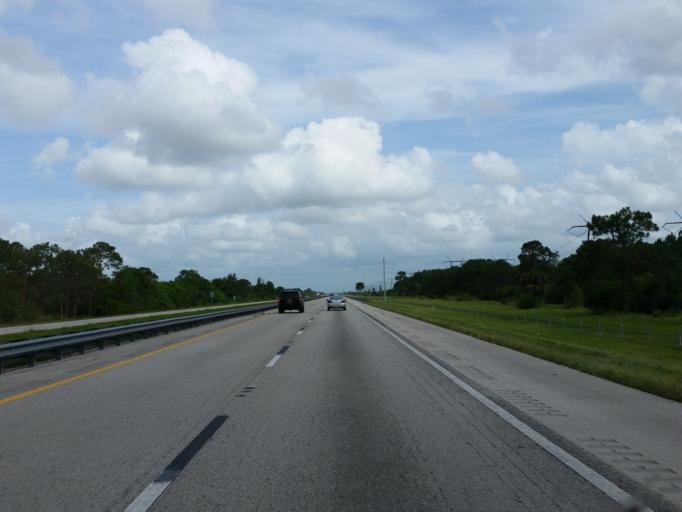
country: US
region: Florida
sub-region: Indian River County
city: West Vero Corridor
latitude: 27.5228
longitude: -80.5993
